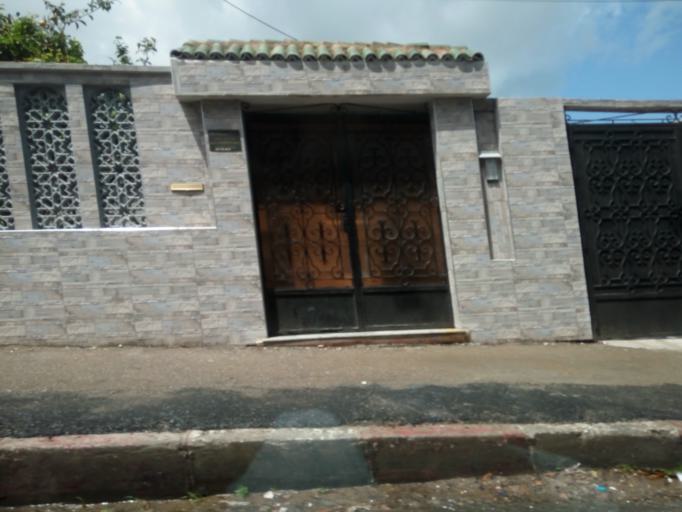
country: DZ
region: Alger
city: Algiers
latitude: 36.7755
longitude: 3.0459
